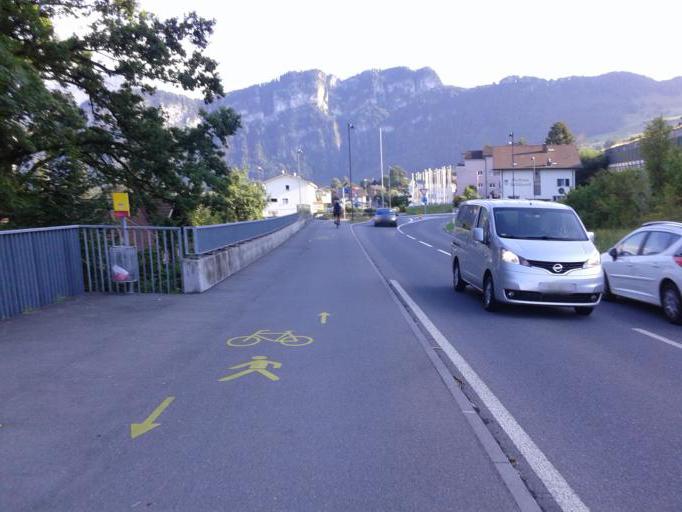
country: CH
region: Nidwalden
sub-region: Nidwalden
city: Hergiswil
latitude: 46.9988
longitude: 8.3118
